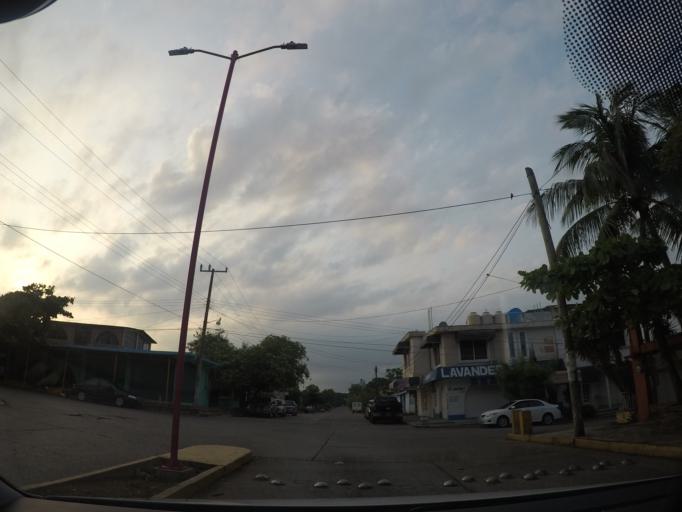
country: MX
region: Oaxaca
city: Matias Romero
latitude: 16.8751
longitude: -95.0370
